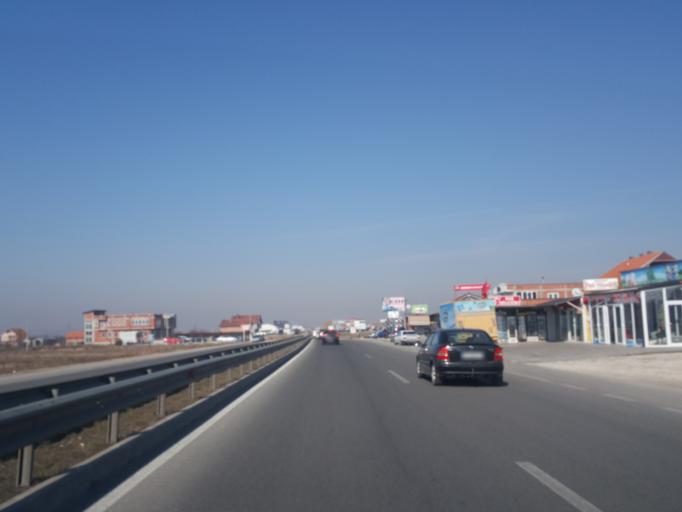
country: XK
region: Pristina
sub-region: Komuna e Obiliqit
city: Obiliq
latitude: 42.7620
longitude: 21.0294
